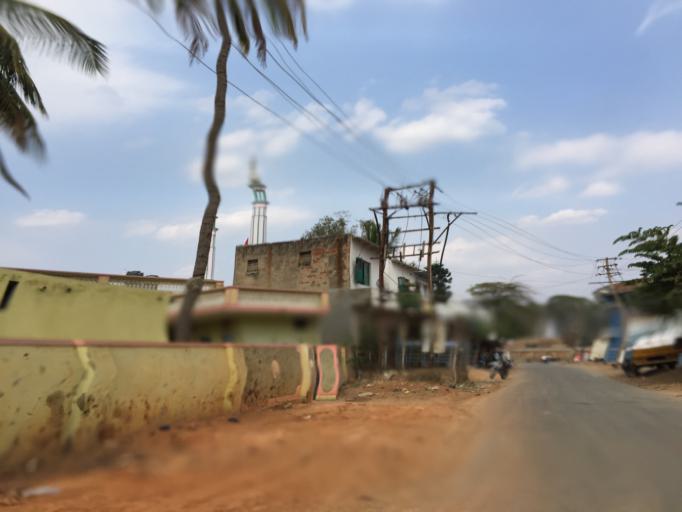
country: IN
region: Karnataka
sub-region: Chikkaballapur
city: Chik Ballapur
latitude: 13.3859
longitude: 77.6969
